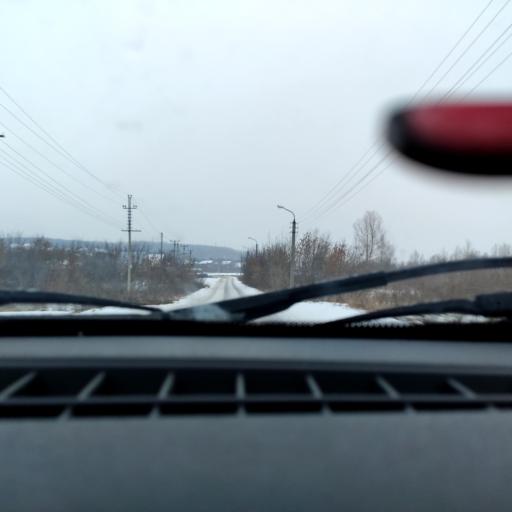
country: RU
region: Bashkortostan
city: Blagoveshchensk
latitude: 54.8910
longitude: 56.0335
